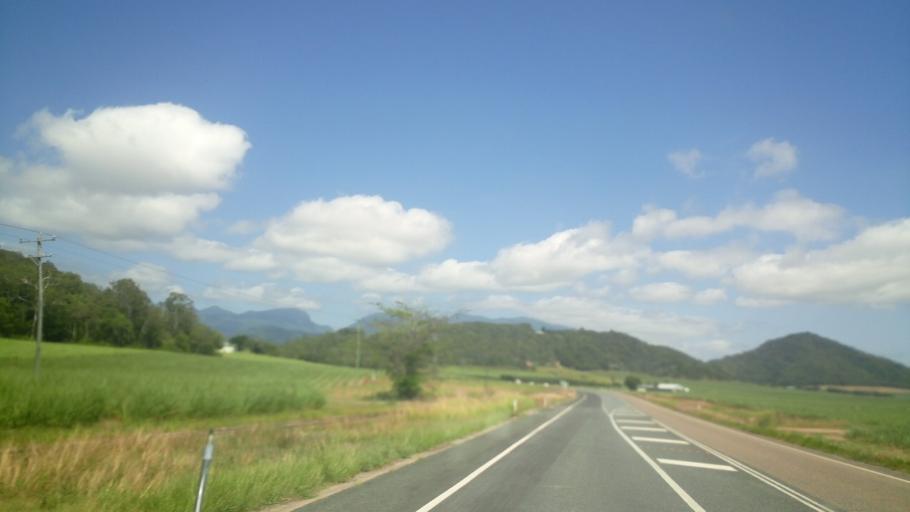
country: AU
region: Queensland
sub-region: Cairns
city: Port Douglas
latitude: -16.4802
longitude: 145.4064
